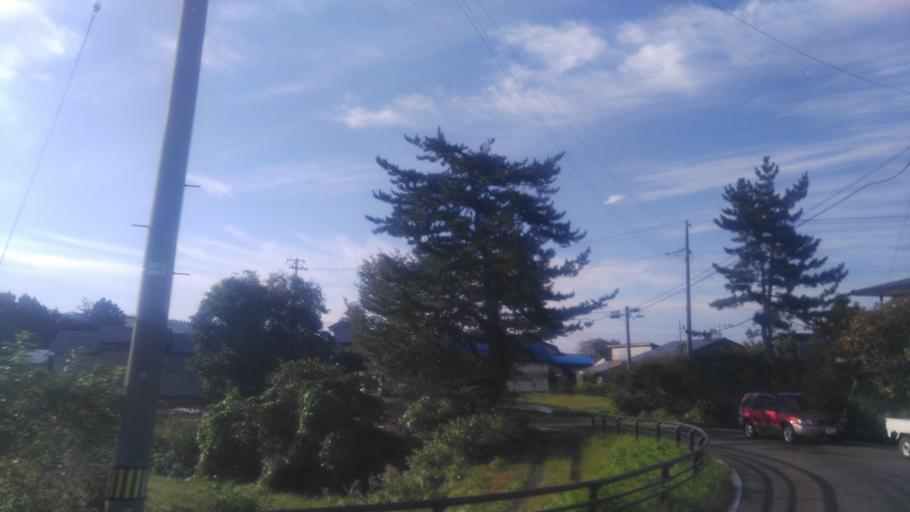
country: JP
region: Akita
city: Takanosu
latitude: 40.2575
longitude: 140.4001
